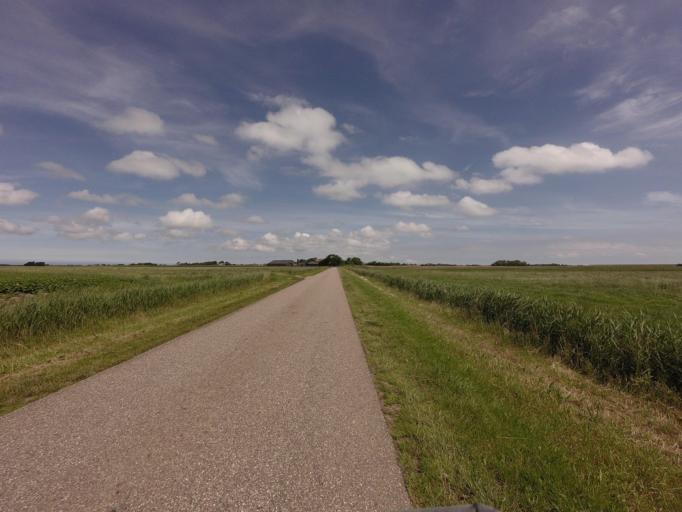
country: NL
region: North Holland
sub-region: Gemeente Texel
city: Den Burg
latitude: 53.0619
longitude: 4.8500
